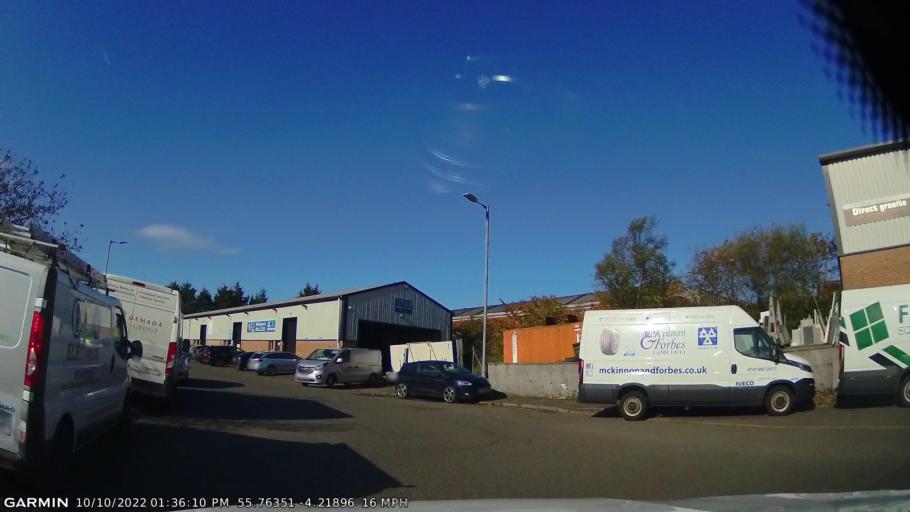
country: GB
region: Scotland
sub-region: Glasgow City
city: Carmunnock
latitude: 55.7634
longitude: -4.2189
